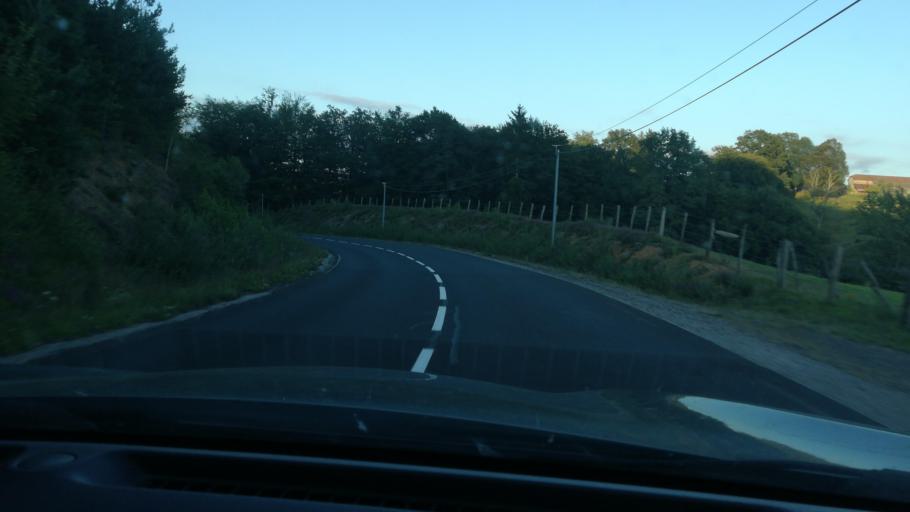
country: FR
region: Auvergne
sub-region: Departement du Cantal
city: Laroquebrou
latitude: 44.9227
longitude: 2.0728
